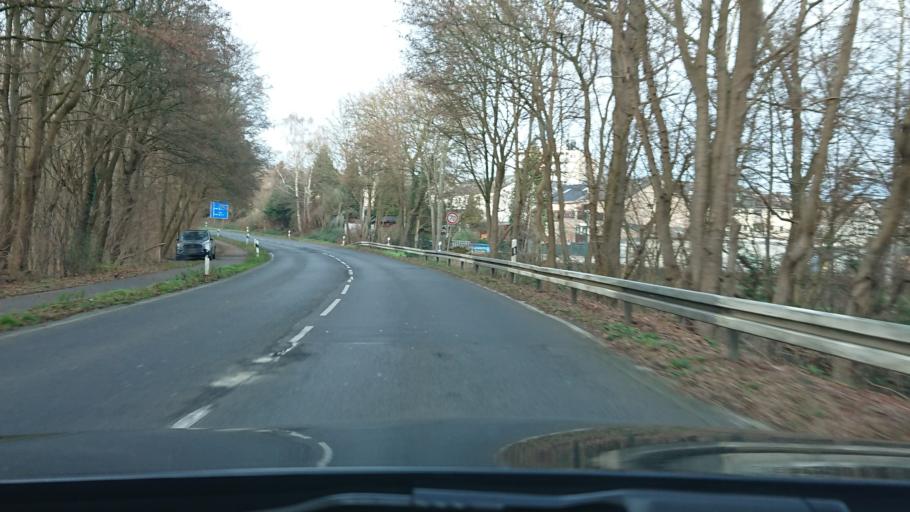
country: DE
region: North Rhine-Westphalia
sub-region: Regierungsbezirk Koln
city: Frechen
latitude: 50.8850
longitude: 6.8224
